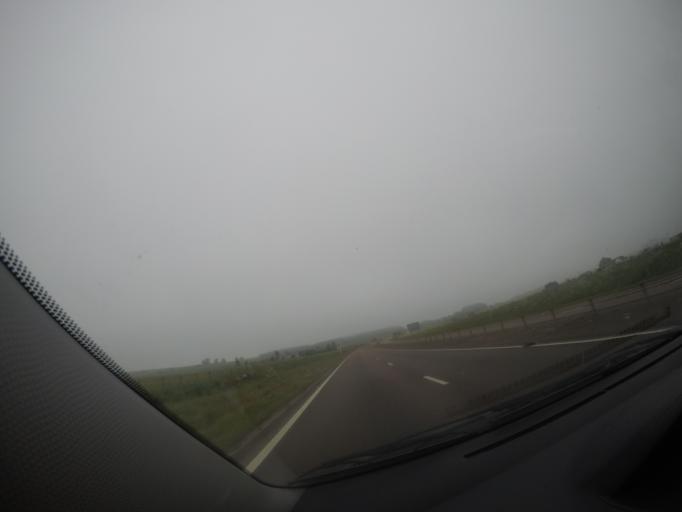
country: GB
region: Scotland
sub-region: Dundee City
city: Dundee
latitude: 56.5385
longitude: -2.9462
